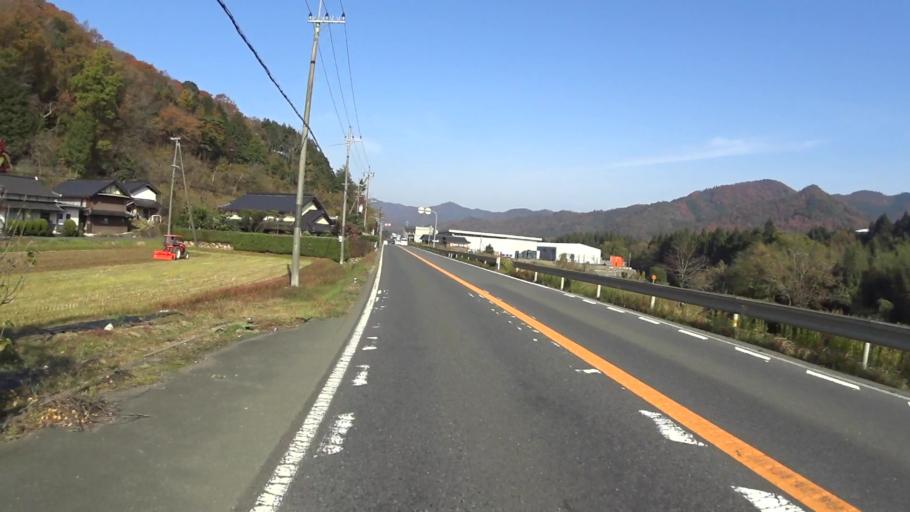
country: JP
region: Kyoto
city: Ayabe
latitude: 35.2368
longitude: 135.2190
